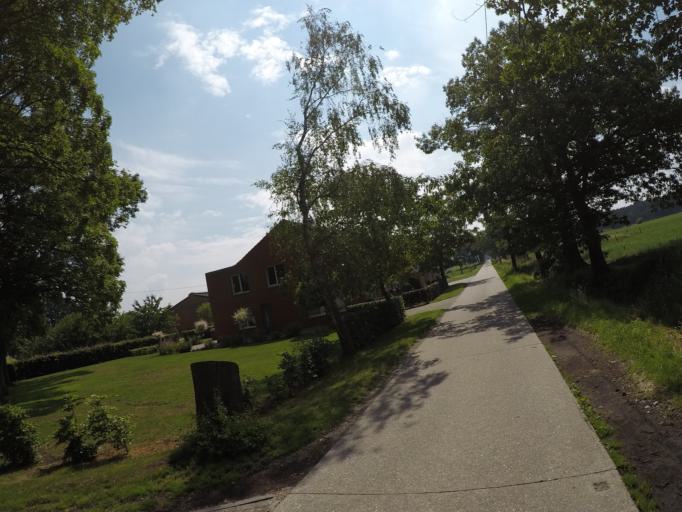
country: BE
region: Flanders
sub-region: Provincie Antwerpen
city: Wuustwezel
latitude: 51.3365
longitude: 4.5765
